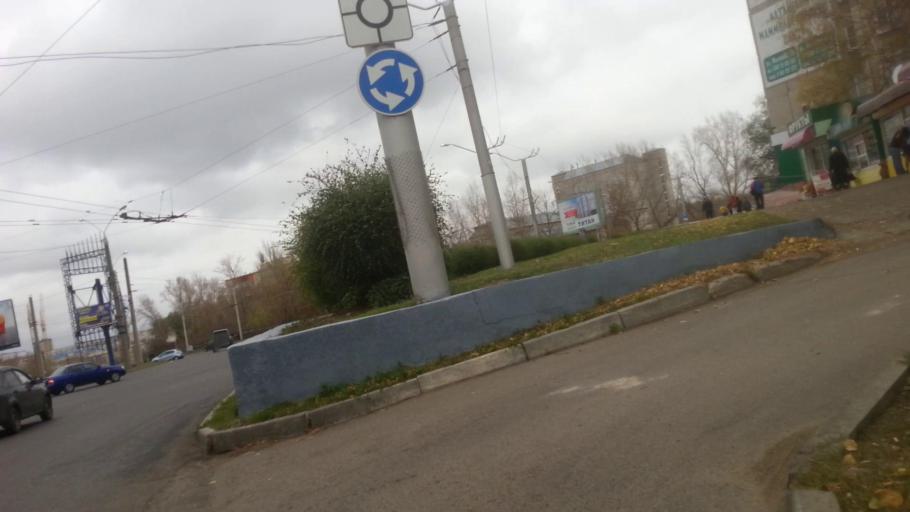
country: RU
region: Altai Krai
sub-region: Gorod Barnaulskiy
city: Barnaul
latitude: 53.3670
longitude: 83.7071
